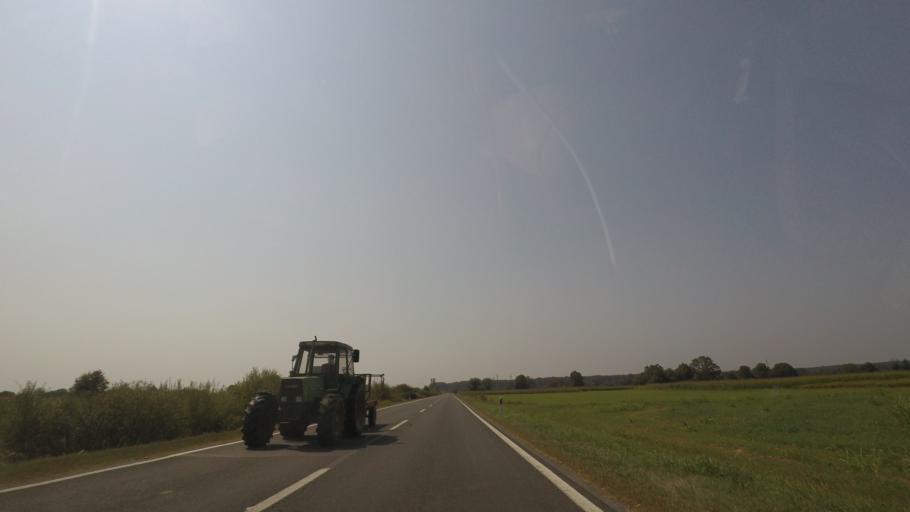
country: HR
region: Sisacko-Moslavacka
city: Novska
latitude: 45.3461
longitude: 16.9603
